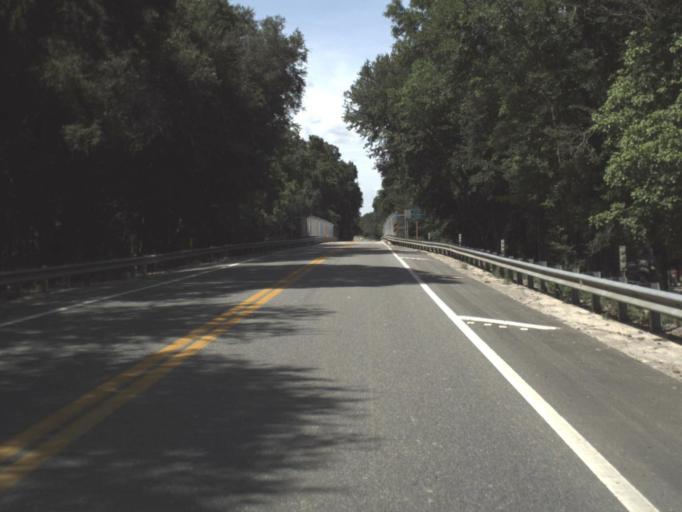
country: US
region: Florida
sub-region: Alachua County
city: High Springs
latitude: 29.8638
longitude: -82.7406
